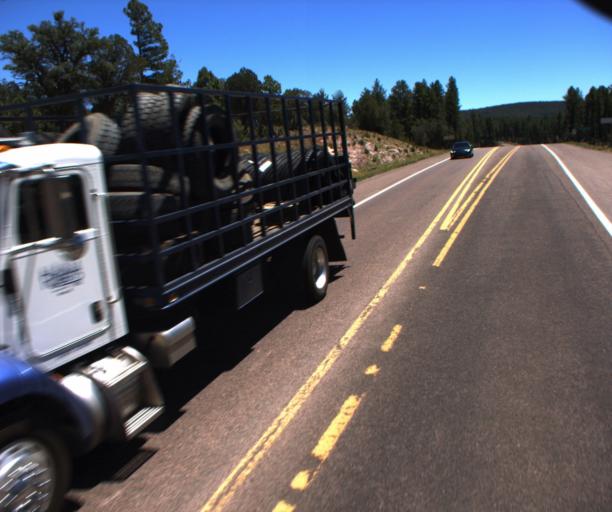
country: US
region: Arizona
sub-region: Gila County
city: Pine
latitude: 34.3773
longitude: -111.4493
